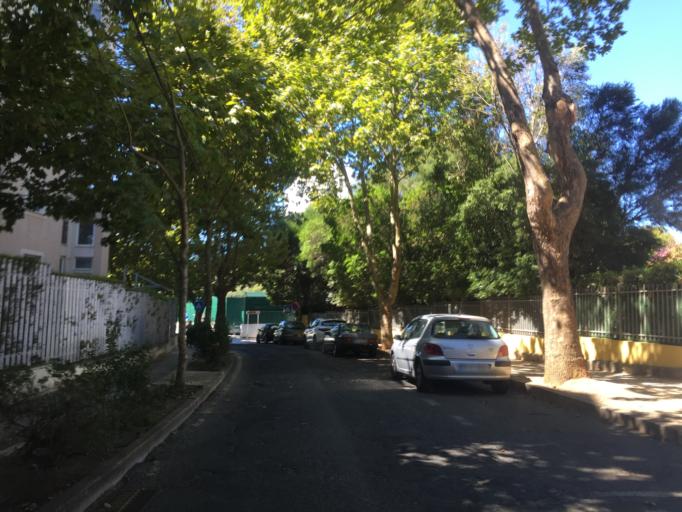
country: PT
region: Lisbon
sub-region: Cascais
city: Cascais
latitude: 38.6992
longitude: -9.4295
